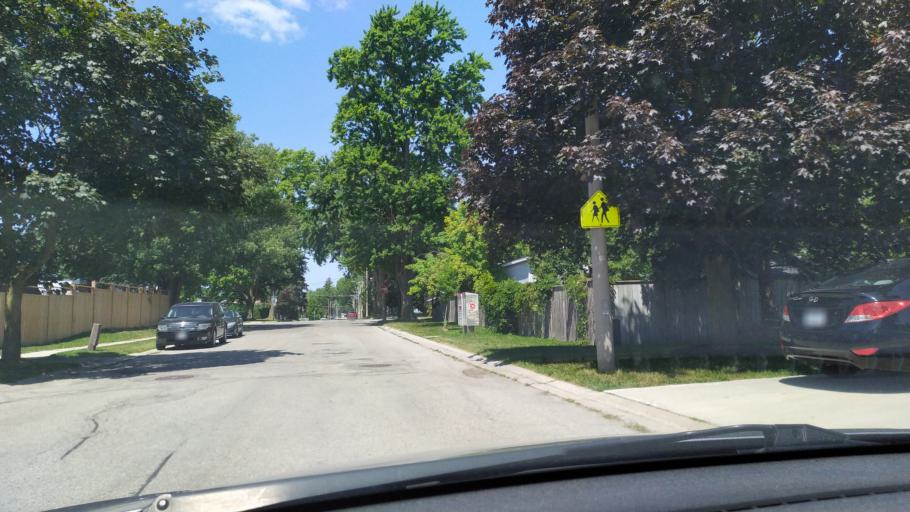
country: CA
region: Ontario
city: Stratford
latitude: 43.3561
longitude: -80.9821
